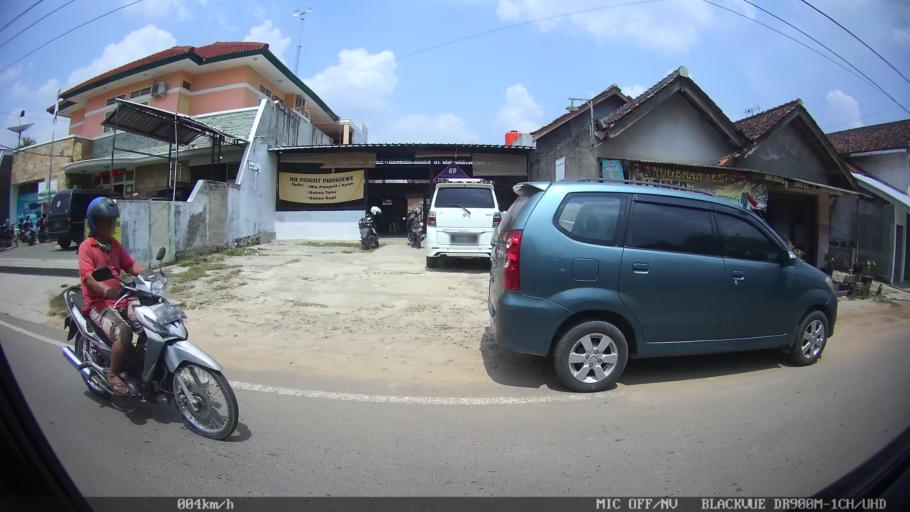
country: ID
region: Lampung
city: Pringsewu
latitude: -5.3595
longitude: 104.9771
